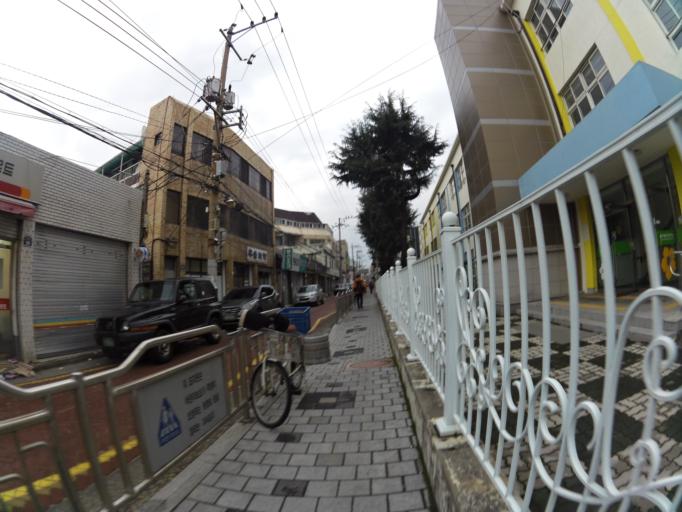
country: KR
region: Daegu
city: Daegu
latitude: 35.8726
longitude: 128.5906
